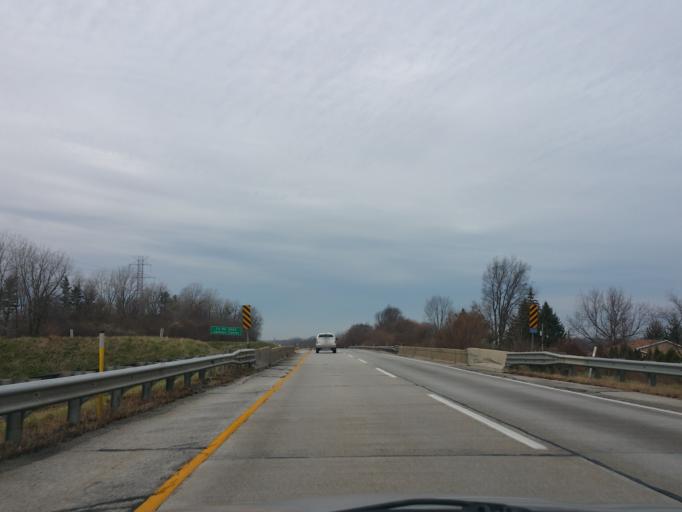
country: US
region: Indiana
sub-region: Porter County
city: Chesterton
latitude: 41.5709
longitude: -86.9981
